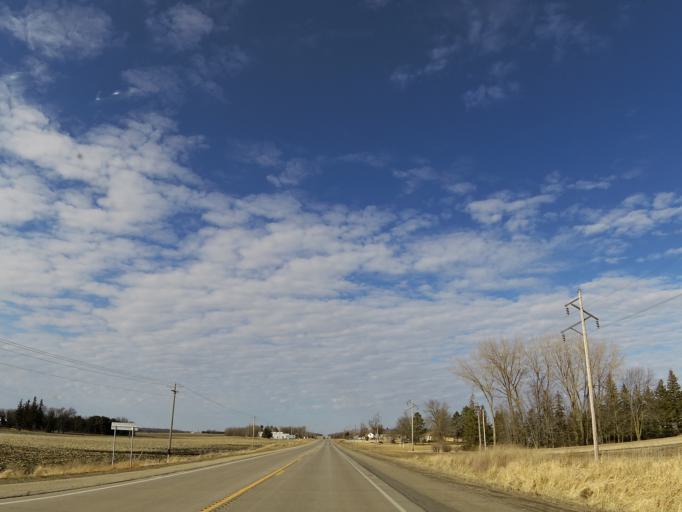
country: US
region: Minnesota
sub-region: Le Sueur County
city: Montgomery
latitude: 44.4888
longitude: -93.5855
